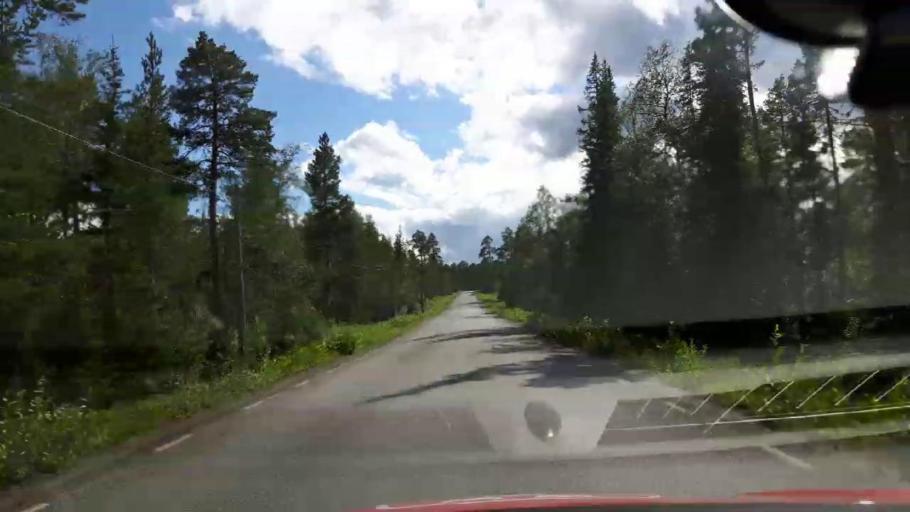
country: SE
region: Jaemtland
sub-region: Are Kommun
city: Are
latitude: 63.1898
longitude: 13.1306
